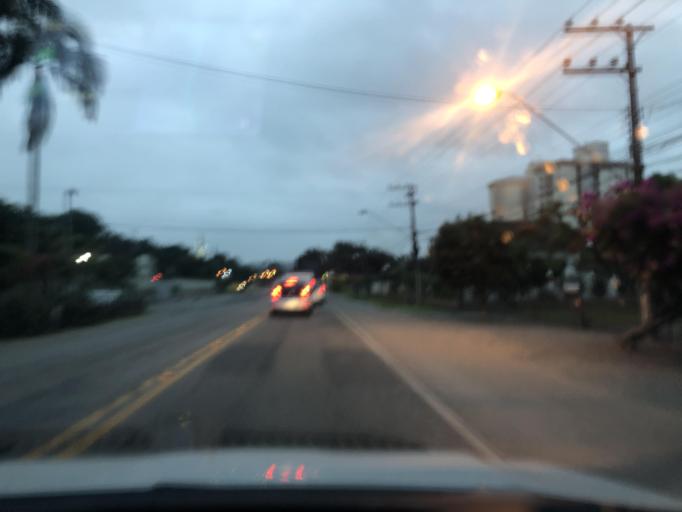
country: BR
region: Santa Catarina
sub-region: Pomerode
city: Pomerode
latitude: -26.7905
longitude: -49.0866
